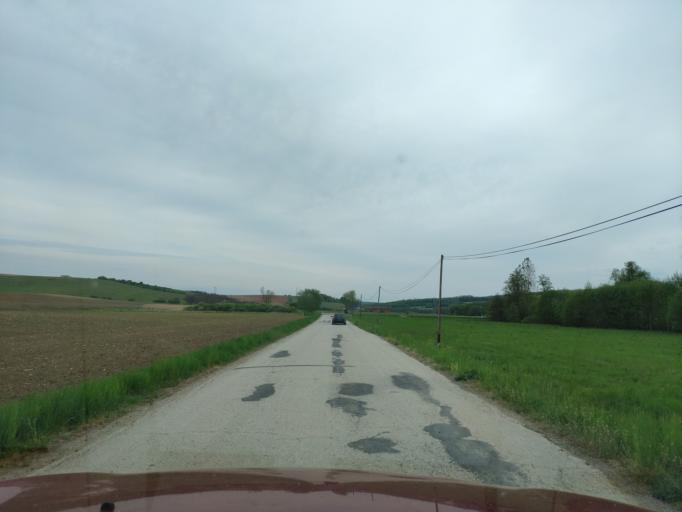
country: SK
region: Banskobystricky
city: Revuca
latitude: 48.4968
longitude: 20.2113
